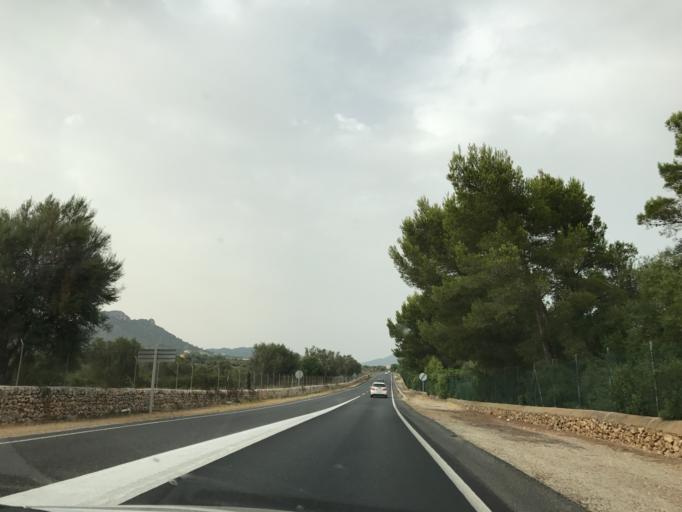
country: ES
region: Balearic Islands
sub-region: Illes Balears
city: Son Servera
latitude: 39.5851
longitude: 3.3648
